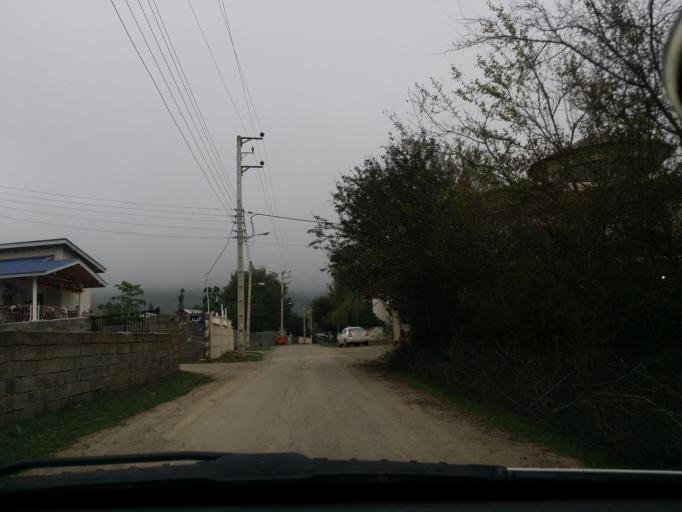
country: IR
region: Mazandaran
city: Chalus
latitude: 36.5116
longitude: 51.2263
